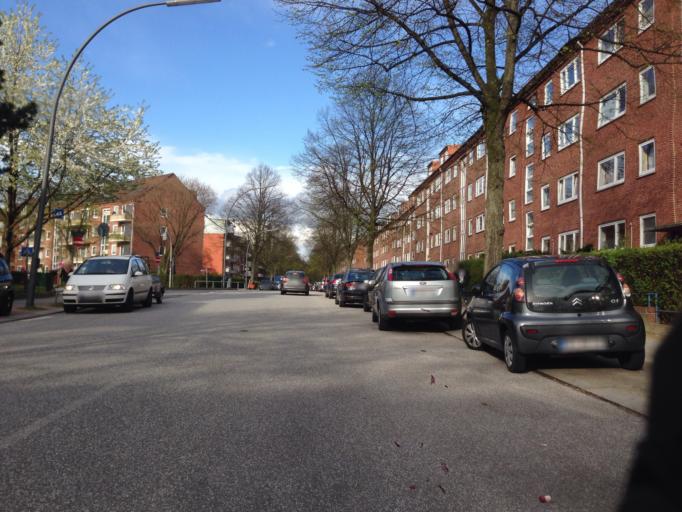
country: DE
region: Hamburg
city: Borgfelde
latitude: 53.5619
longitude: 10.0379
